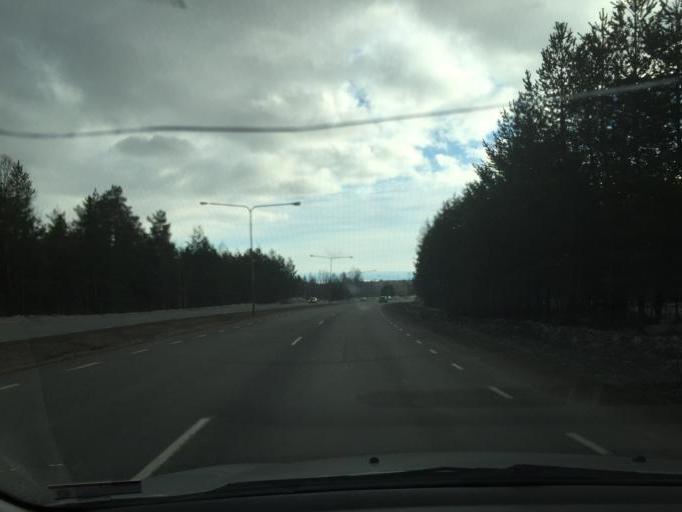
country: SE
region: Norrbotten
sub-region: Lulea Kommun
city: Lulea
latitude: 65.5876
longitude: 22.2249
